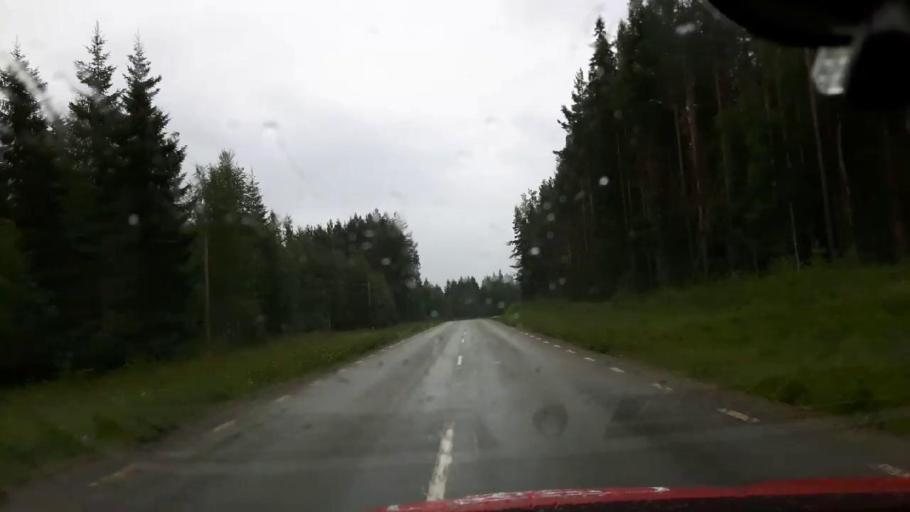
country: SE
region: Jaemtland
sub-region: OEstersunds Kommun
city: Brunflo
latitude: 62.8338
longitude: 15.0071
